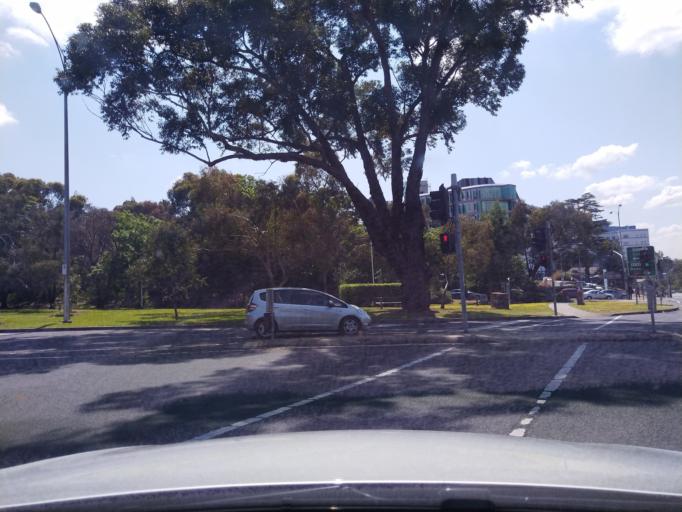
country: AU
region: Victoria
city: Rosanna
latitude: -37.7587
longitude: 145.0583
